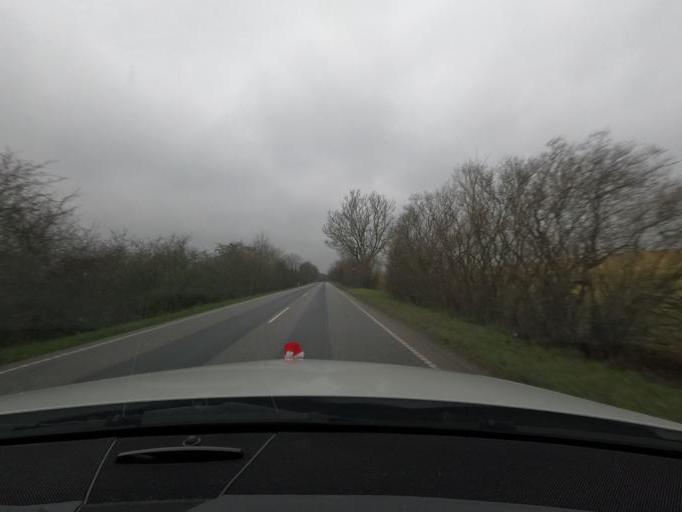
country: DK
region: South Denmark
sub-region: Haderslev Kommune
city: Starup
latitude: 55.2106
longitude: 9.5831
